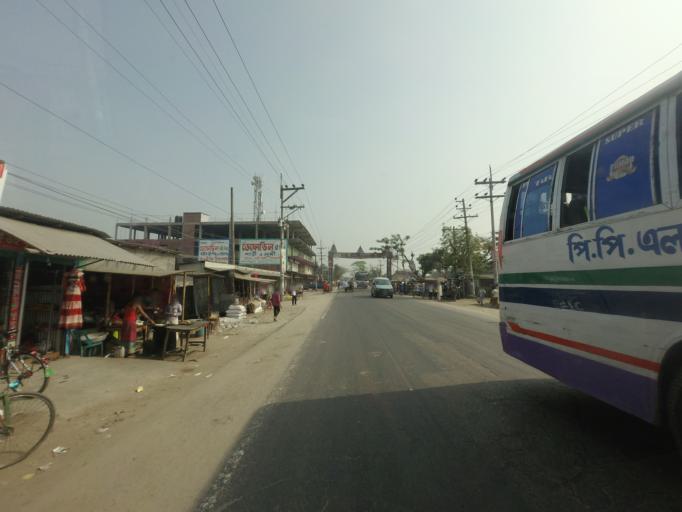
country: BD
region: Dhaka
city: Narsingdi
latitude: 23.8143
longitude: 90.5949
